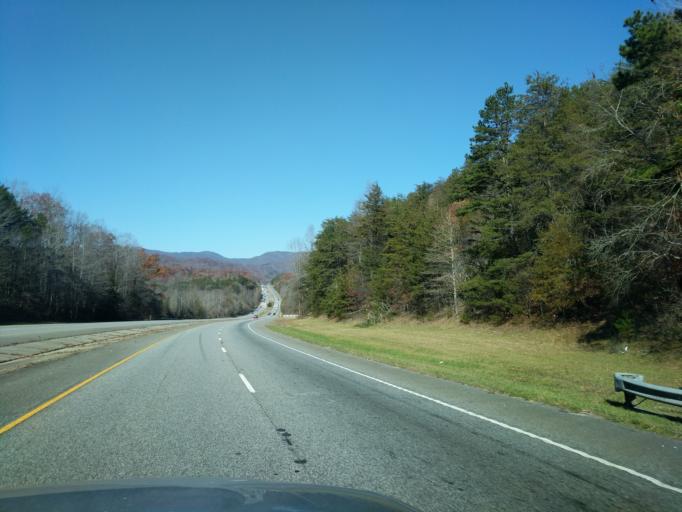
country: US
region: South Carolina
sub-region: Greenville County
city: Slater-Marietta
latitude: 35.1045
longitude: -82.4529
